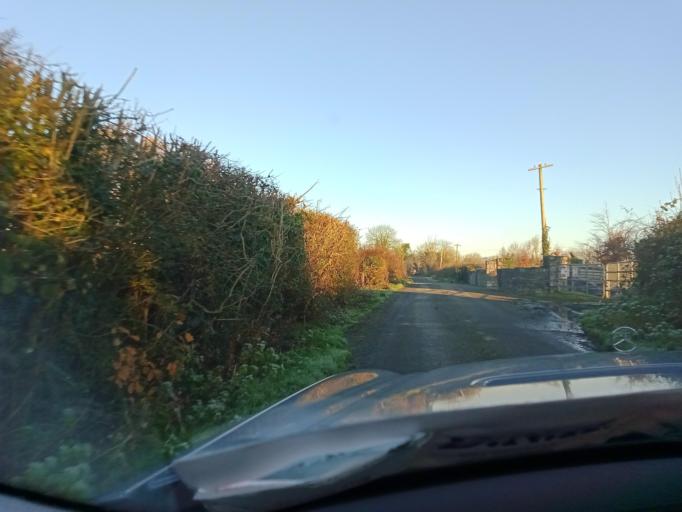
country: IE
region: Leinster
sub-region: Kilkenny
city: Callan
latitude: 52.5183
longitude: -7.4467
